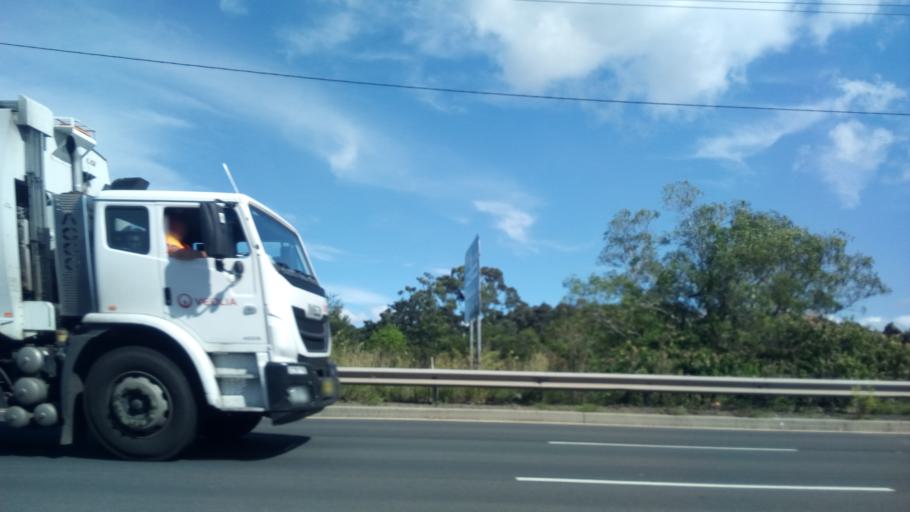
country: AU
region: New South Wales
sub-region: Wollongong
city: Cordeaux Heights
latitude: -34.4520
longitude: 150.8530
